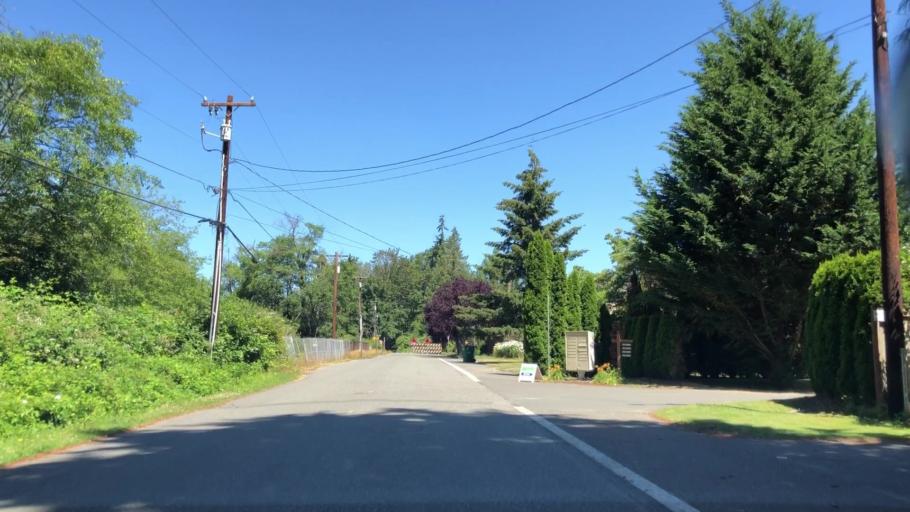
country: US
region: Washington
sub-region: Snohomish County
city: Martha Lake
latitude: 47.8622
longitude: -122.2360
